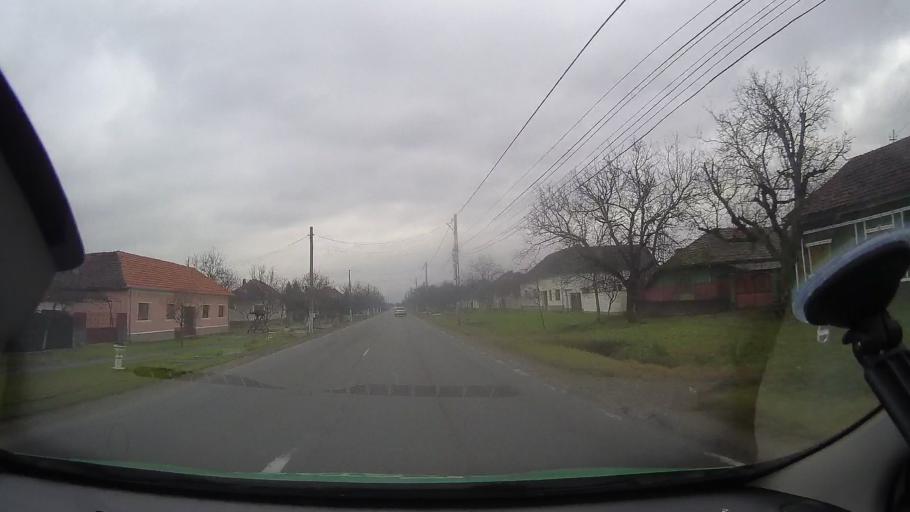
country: RO
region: Arad
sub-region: Comuna Almas
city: Almas
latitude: 46.2828
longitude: 22.2670
